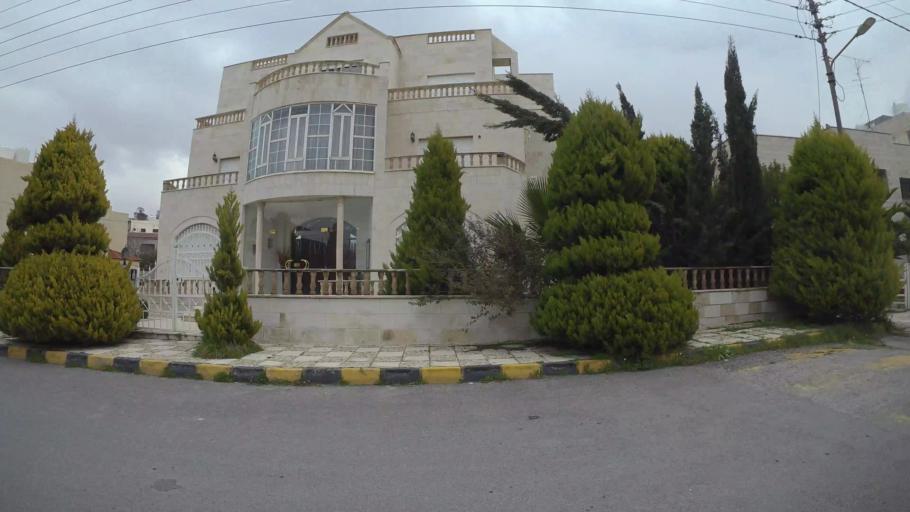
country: JO
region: Amman
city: Umm as Summaq
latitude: 31.8910
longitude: 35.8551
